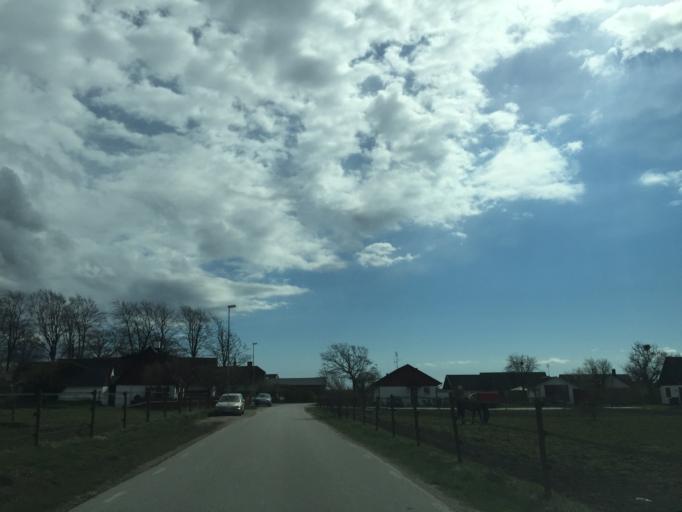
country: SE
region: Skane
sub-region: Vellinge Kommun
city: Hollviken
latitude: 55.4368
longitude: 12.9548
